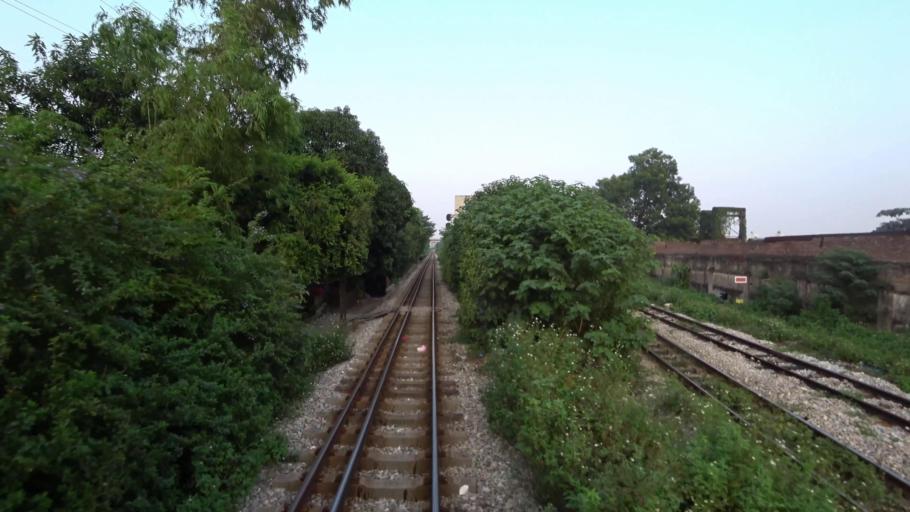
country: VN
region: Ha Noi
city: Trau Quy
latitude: 21.0694
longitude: 105.9006
